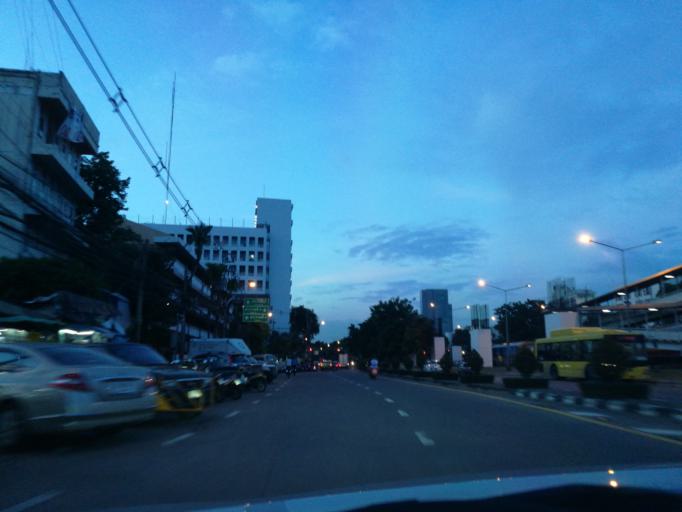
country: TH
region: Bangkok
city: Dusit
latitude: 13.7800
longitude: 100.5299
